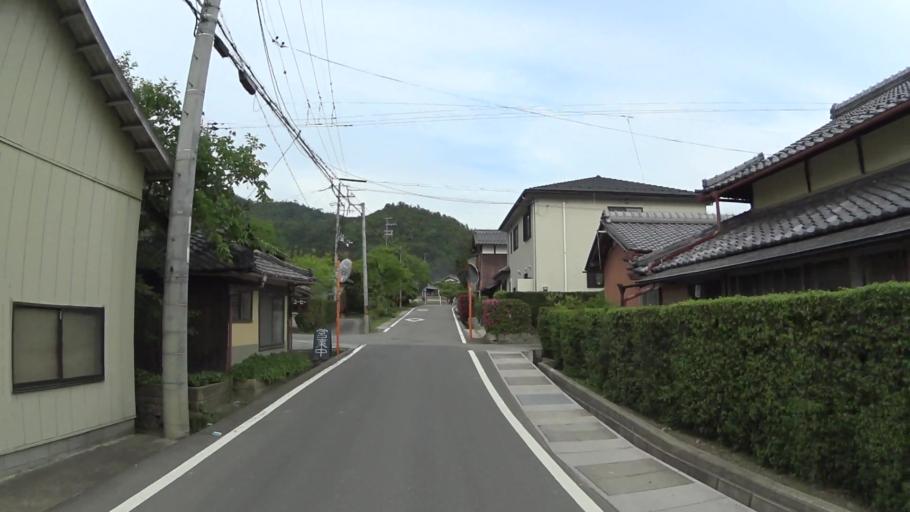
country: JP
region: Kyoto
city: Kameoka
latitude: 35.0915
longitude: 135.5542
